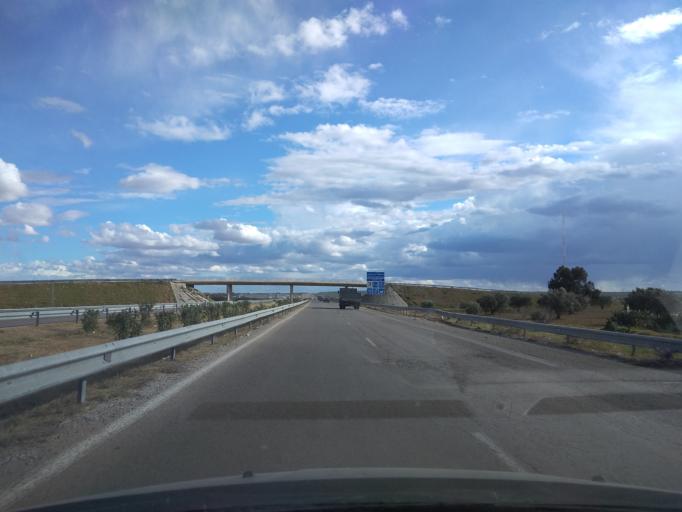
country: TN
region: Al Munastir
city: Manzil Kamil
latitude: 35.5830
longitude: 10.6077
